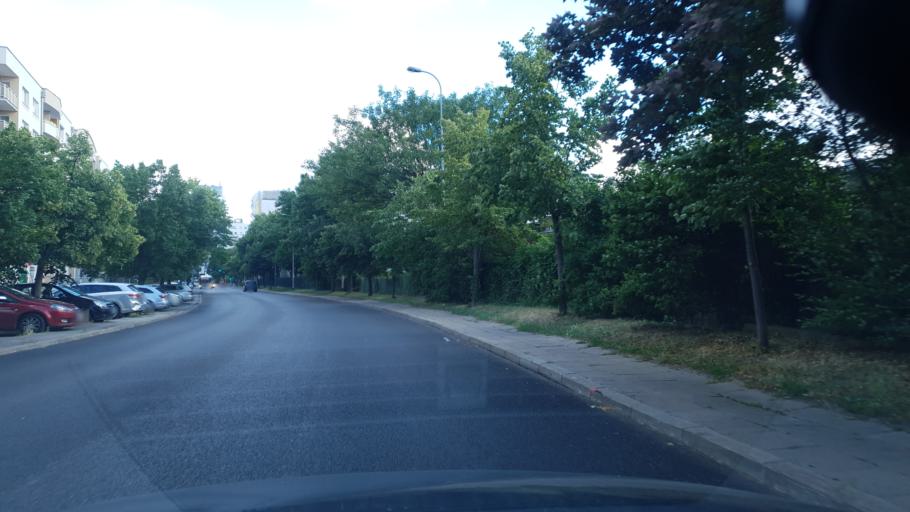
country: PL
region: Pomeranian Voivodeship
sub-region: Gdynia
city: Gdynia
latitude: 54.4951
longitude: 18.5408
